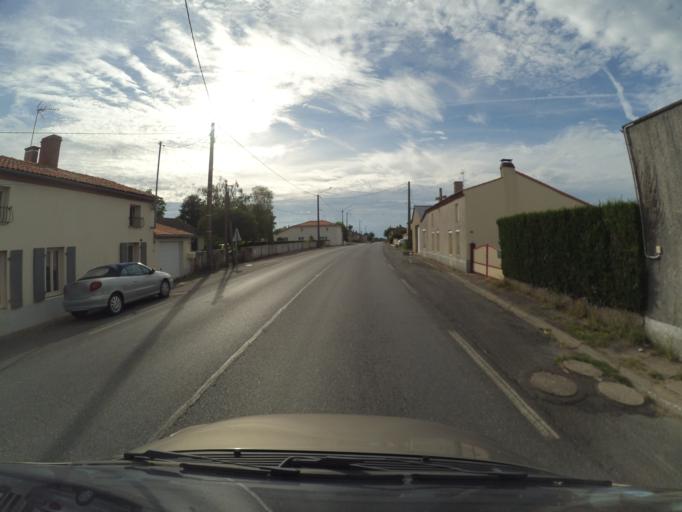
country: FR
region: Poitou-Charentes
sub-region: Departement des Deux-Sevres
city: Saint-Amand-sur-Sevre
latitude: 46.9291
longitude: -0.8165
